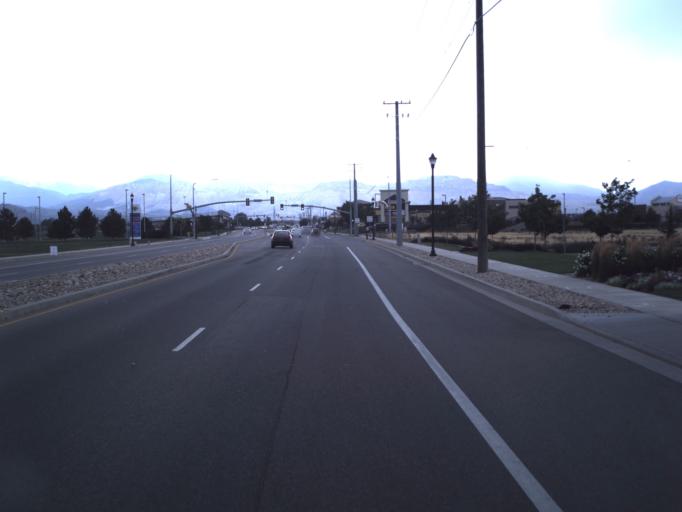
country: US
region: Utah
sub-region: Salt Lake County
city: Riverton
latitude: 40.5223
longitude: -111.9782
